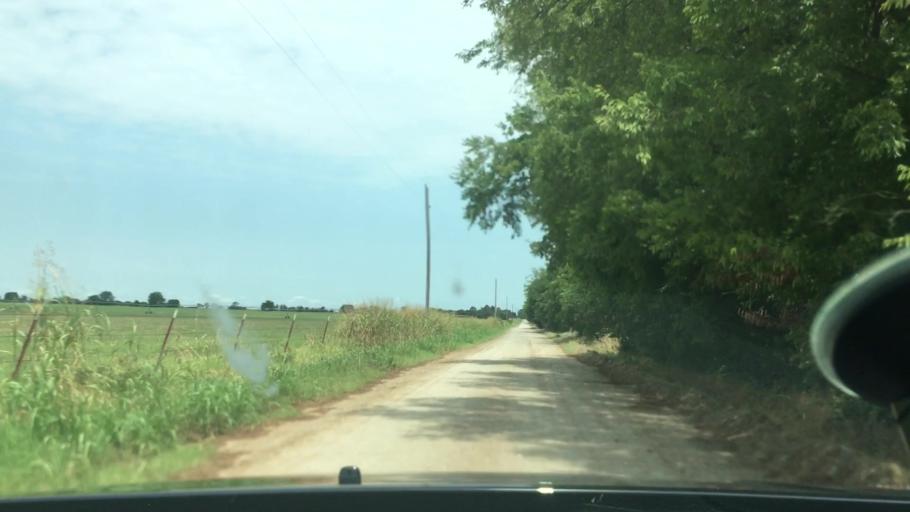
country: US
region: Texas
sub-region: Cooke County
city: Muenster
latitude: 33.8616
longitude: -97.3871
